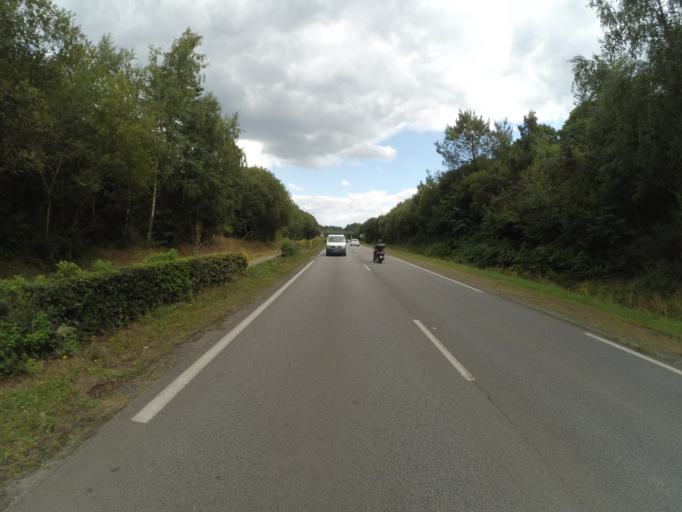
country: FR
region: Brittany
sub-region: Departement du Morbihan
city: Kervignac
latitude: 47.7556
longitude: -3.2396
